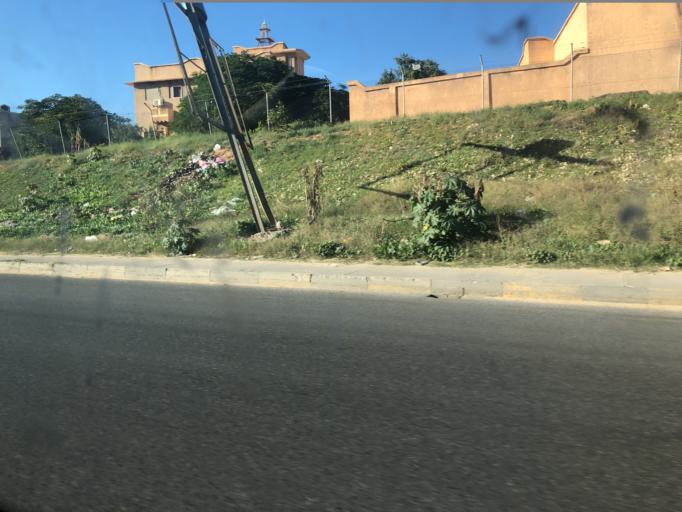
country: LY
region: Tripoli
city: Tripoli
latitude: 32.8690
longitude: 13.2414
